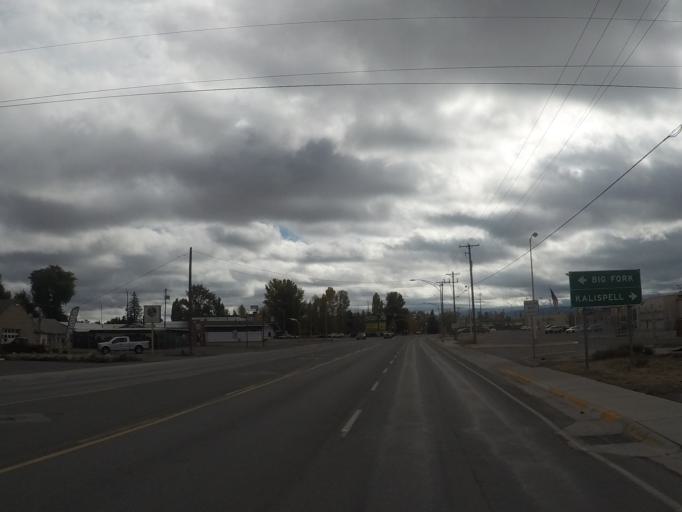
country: US
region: Montana
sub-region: Flathead County
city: Evergreen
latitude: 48.2161
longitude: -114.2773
